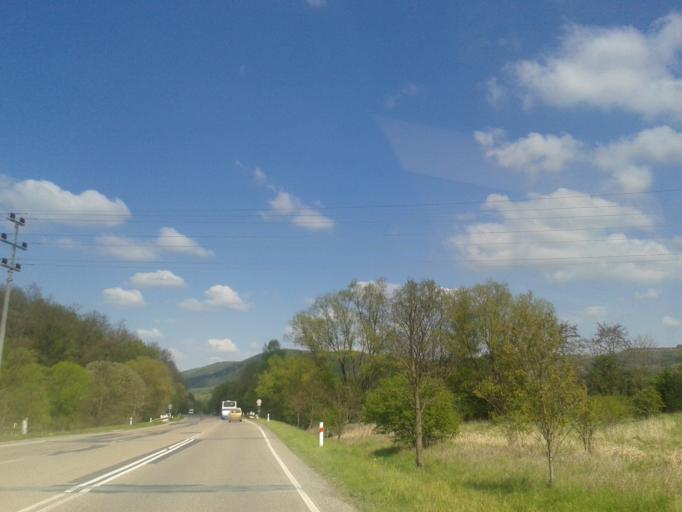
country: CZ
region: Central Bohemia
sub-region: Okres Beroun
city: Lodenice
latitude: 49.9894
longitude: 14.1425
